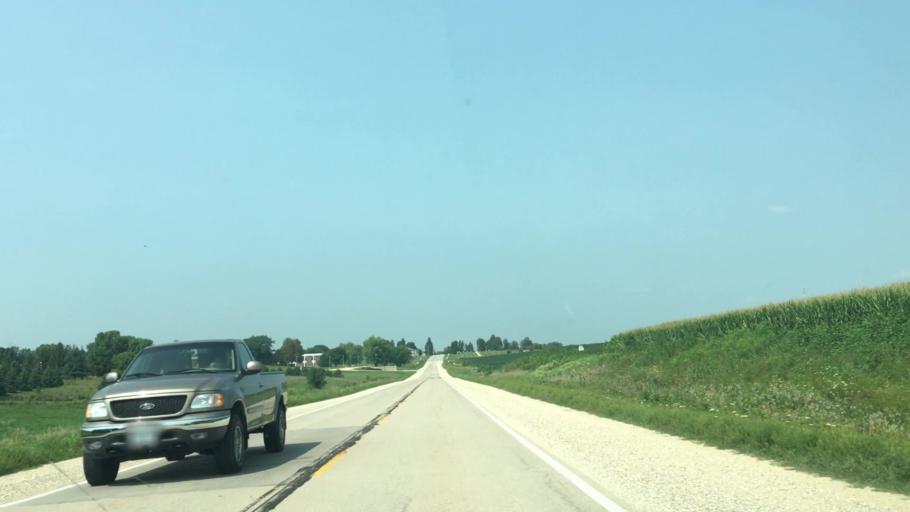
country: US
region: Iowa
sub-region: Winneshiek County
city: Decorah
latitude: 43.1696
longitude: -91.8644
